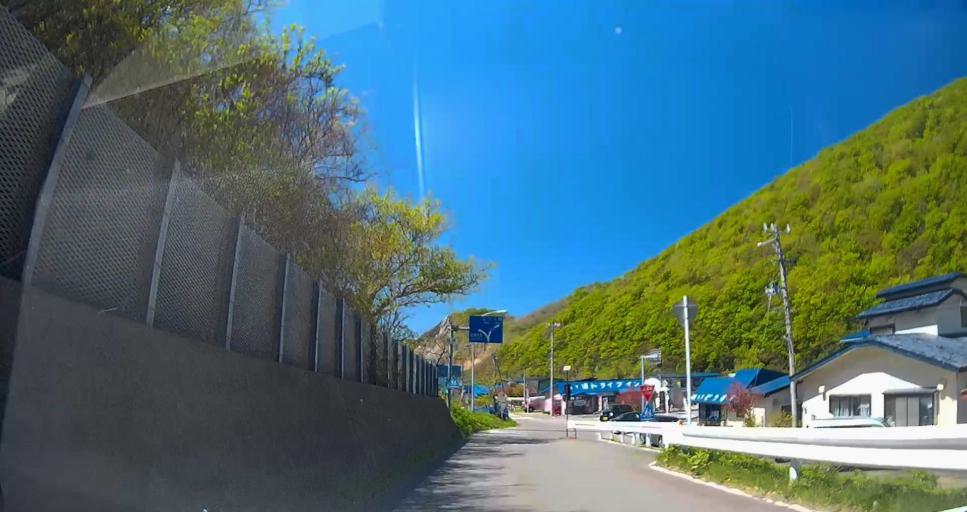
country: JP
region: Aomori
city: Mutsu
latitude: 41.3273
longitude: 140.8124
